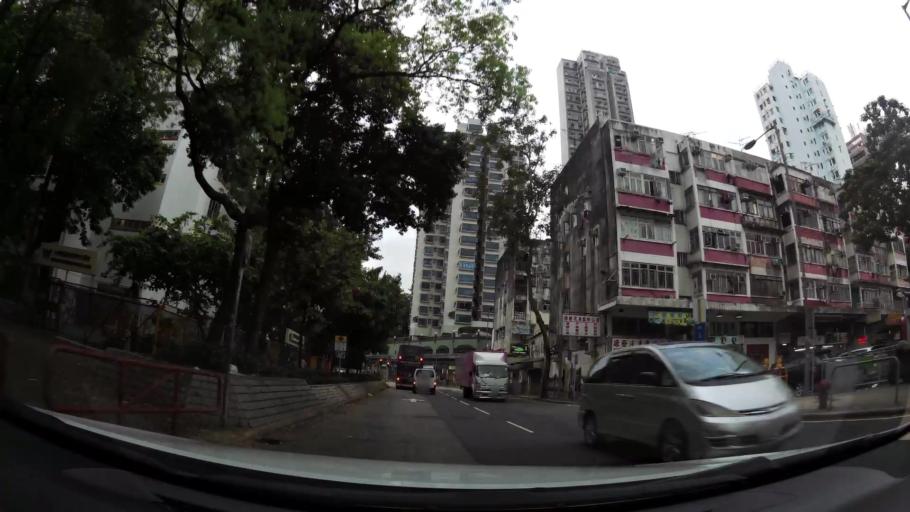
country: HK
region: Tai Po
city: Tai Po
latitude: 22.4487
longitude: 114.1691
